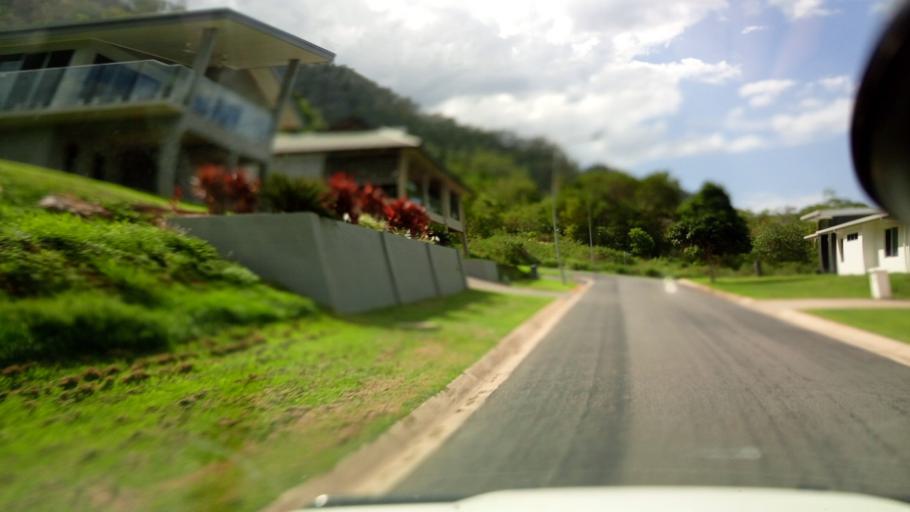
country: AU
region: Queensland
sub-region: Cairns
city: Woree
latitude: -16.9253
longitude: 145.7218
